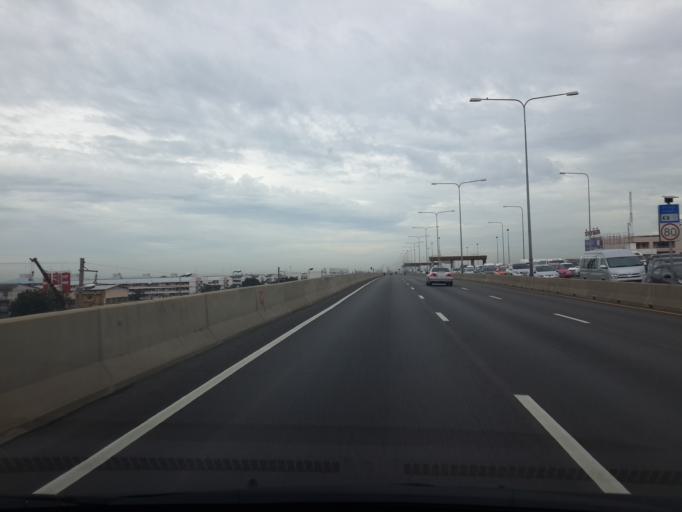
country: TH
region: Bangkok
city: Lak Si
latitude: 13.8956
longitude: 100.5879
